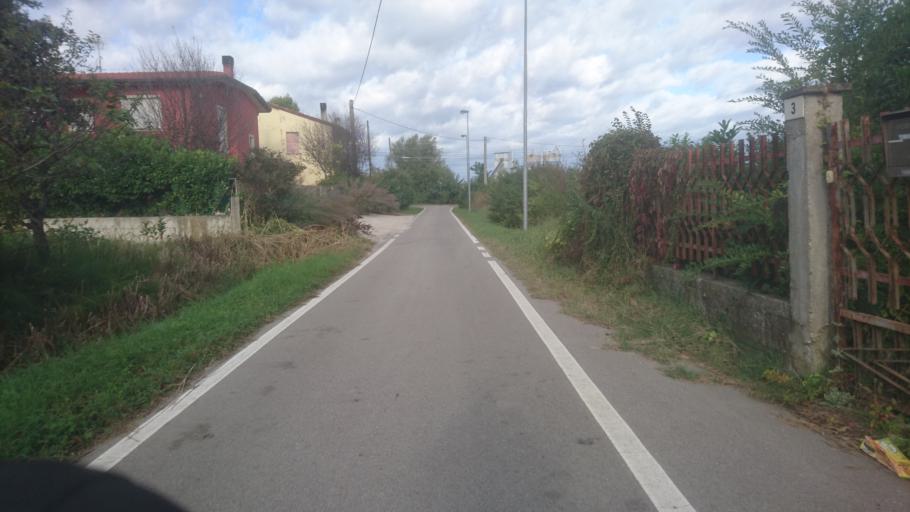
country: IT
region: Veneto
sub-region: Provincia di Padova
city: Abano Terme
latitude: 45.3492
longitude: 11.8089
